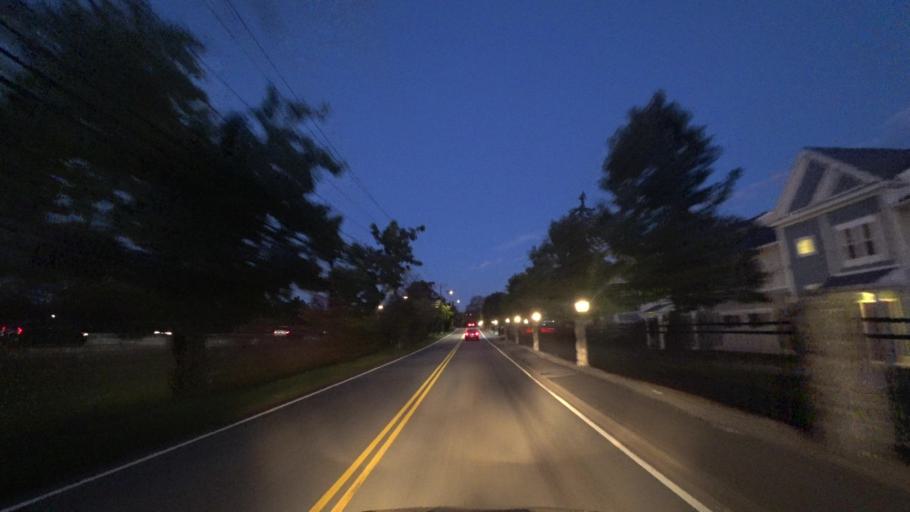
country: US
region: Massachusetts
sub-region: Middlesex County
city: Burlington
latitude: 42.4973
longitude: -71.1722
